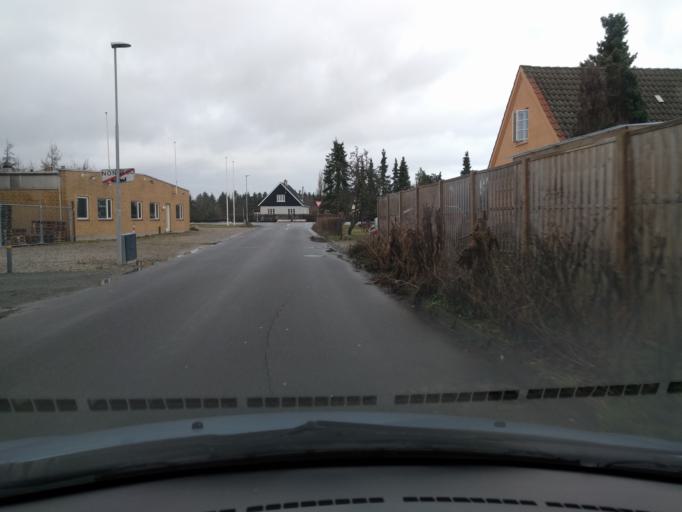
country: DK
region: South Denmark
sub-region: Kerteminde Kommune
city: Langeskov
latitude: 55.3695
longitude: 10.5660
